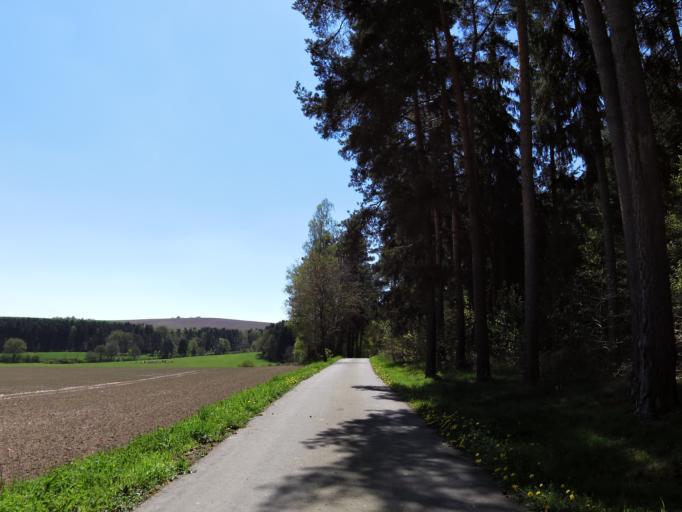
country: DE
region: Thuringia
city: Bad Salzungen
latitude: 50.8361
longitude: 10.2540
